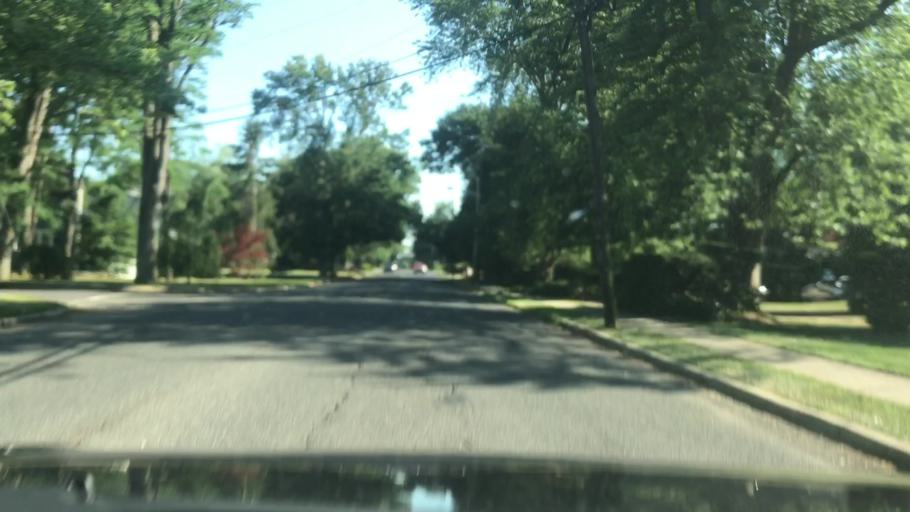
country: US
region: New Jersey
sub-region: Monmouth County
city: Lincroft
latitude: 40.3424
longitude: -74.0958
